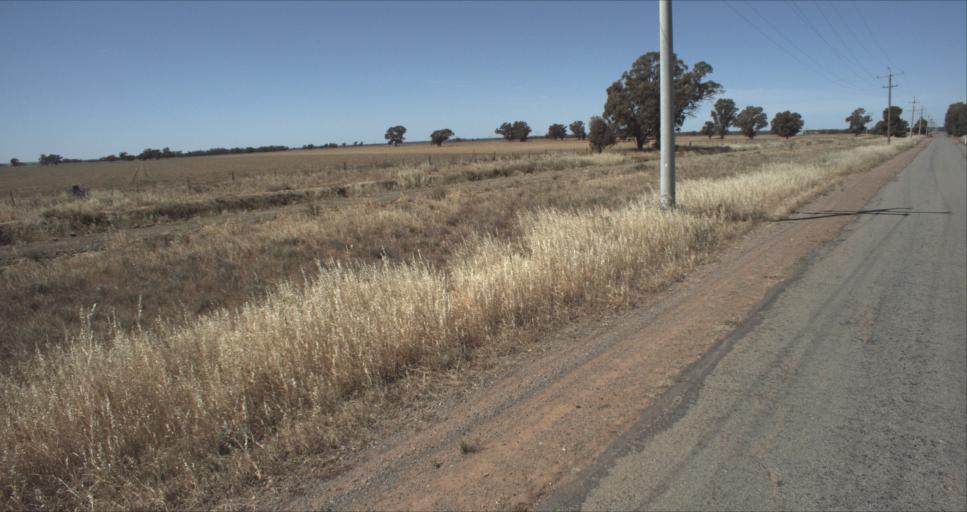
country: AU
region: New South Wales
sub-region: Leeton
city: Leeton
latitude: -34.5698
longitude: 146.3108
